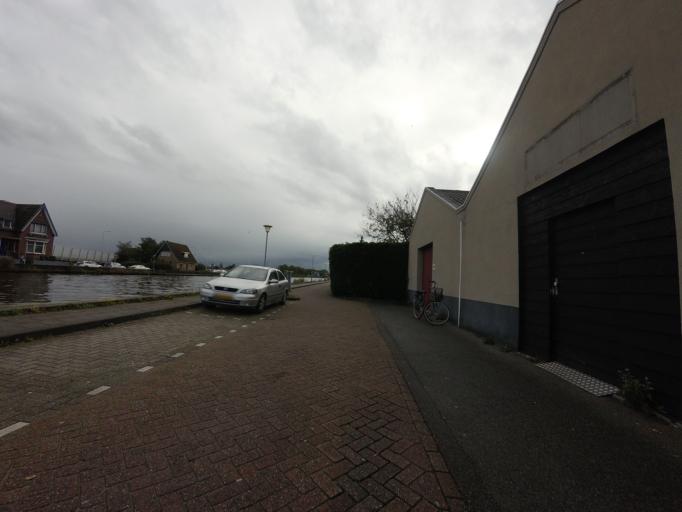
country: NL
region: South Holland
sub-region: Gemeente Boskoop
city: Boskoop
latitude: 52.0848
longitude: 4.6617
